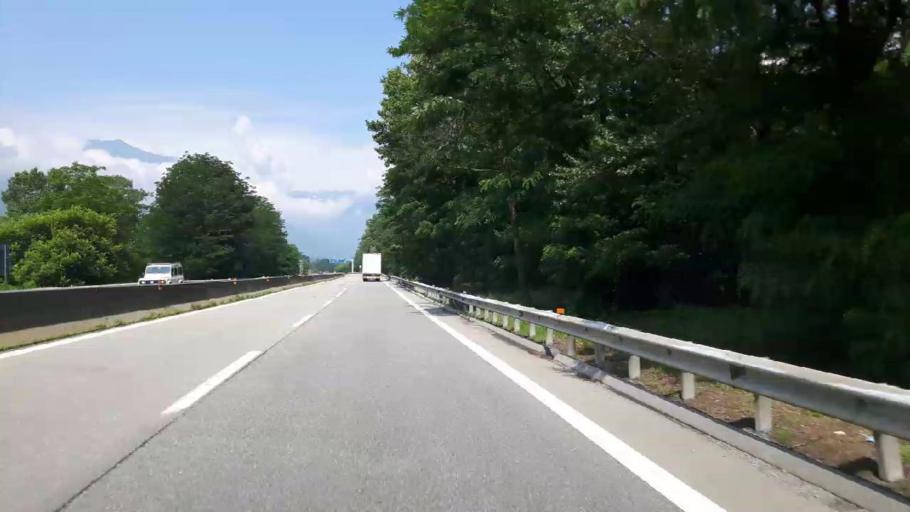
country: IT
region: Piedmont
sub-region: Provincia Verbano-Cusio-Ossola
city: Anzola d'Ossola
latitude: 45.9890
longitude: 8.3611
